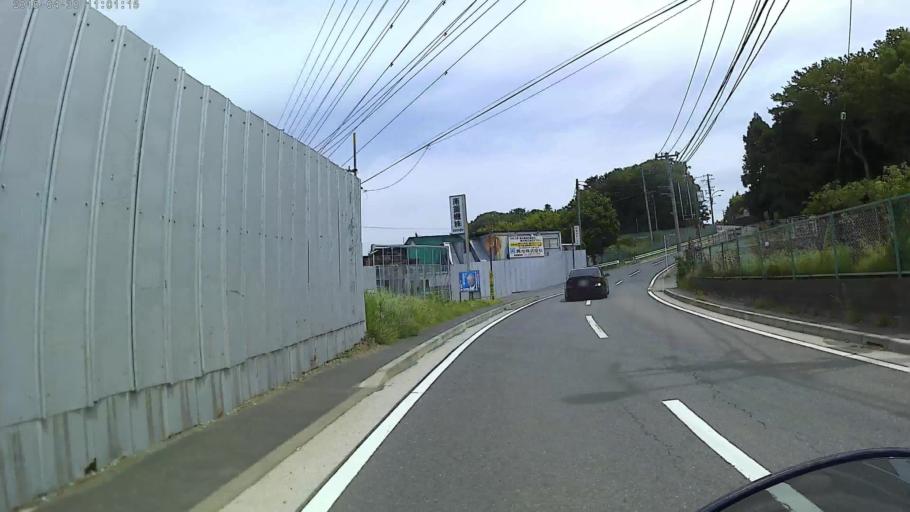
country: JP
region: Kanagawa
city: Minami-rinkan
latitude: 35.4460
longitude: 139.4277
